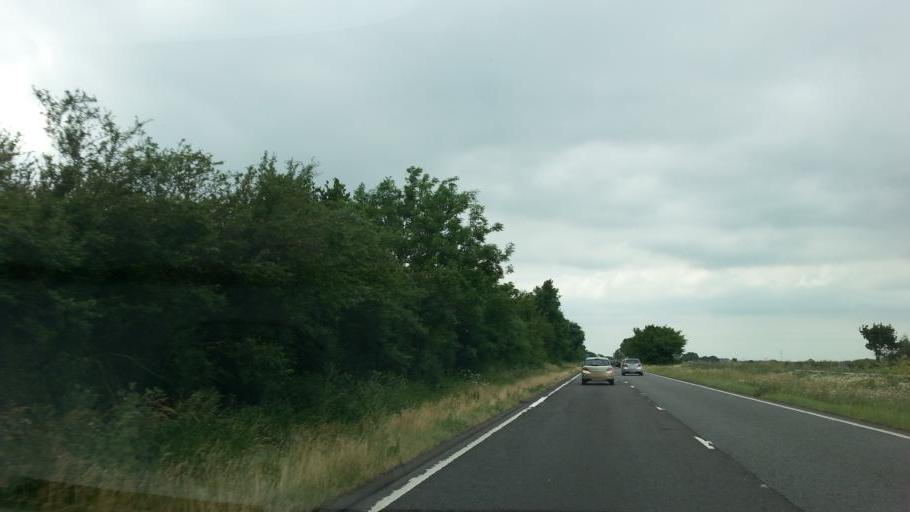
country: GB
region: England
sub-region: District of Rutland
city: Greetham
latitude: 52.7535
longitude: -0.6071
